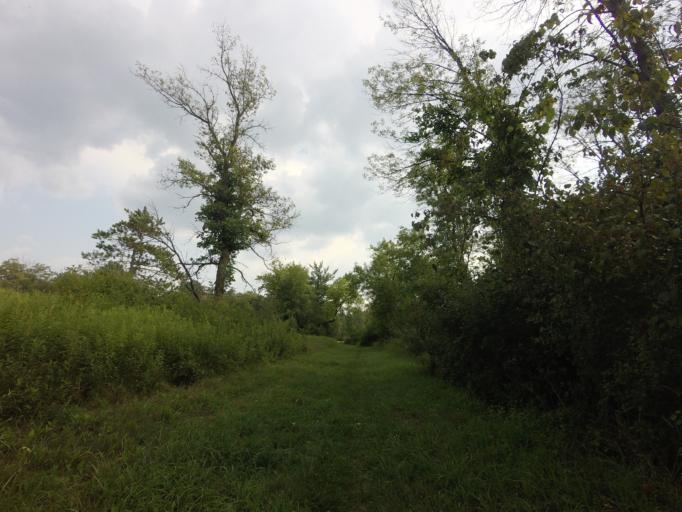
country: US
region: Wisconsin
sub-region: Washington County
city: Kewaskum
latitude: 43.5931
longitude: -88.1765
